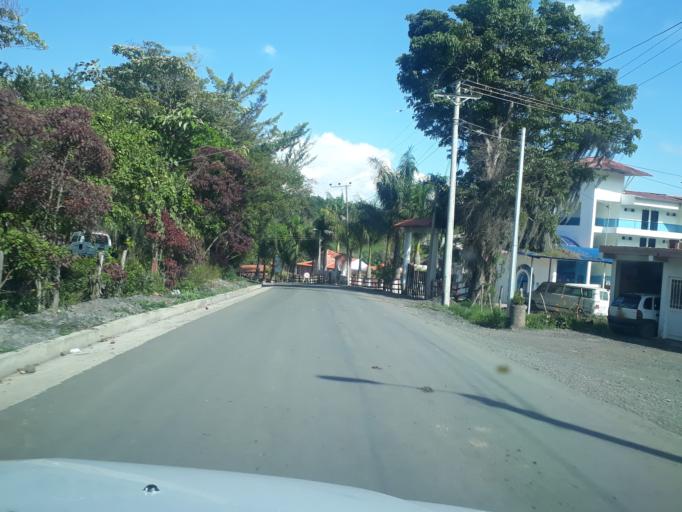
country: CO
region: Santander
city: Velez
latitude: 6.0591
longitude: -73.6416
